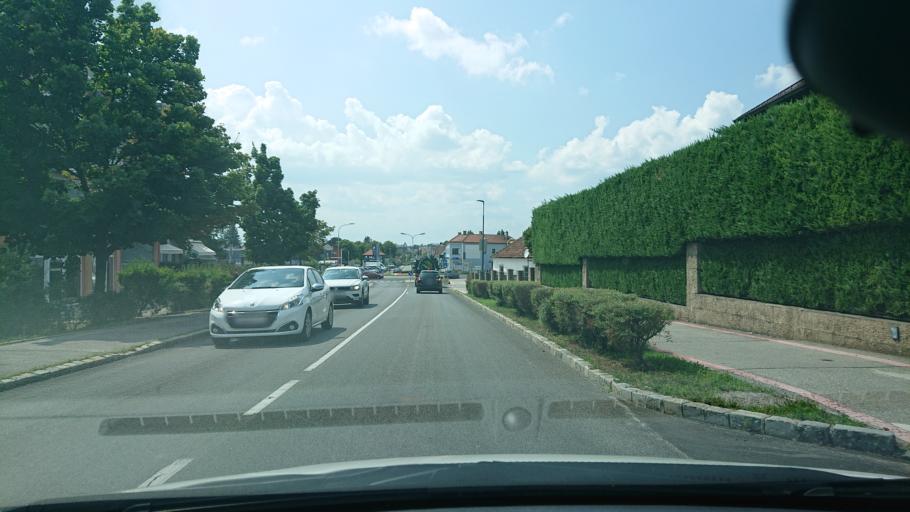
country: AT
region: Lower Austria
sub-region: Politischer Bezirk Baden
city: Leobersdorf
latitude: 47.9359
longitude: 16.2194
